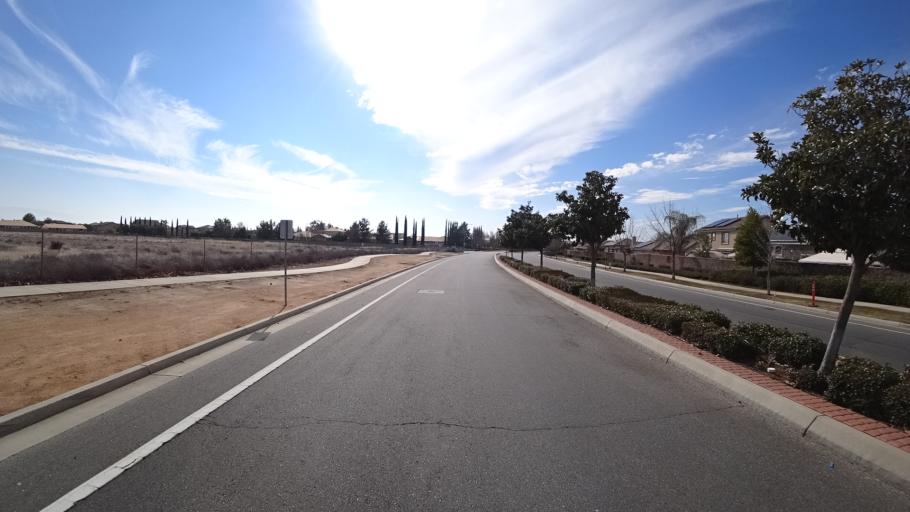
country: US
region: California
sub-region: Kern County
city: Oildale
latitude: 35.4052
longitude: -118.8873
